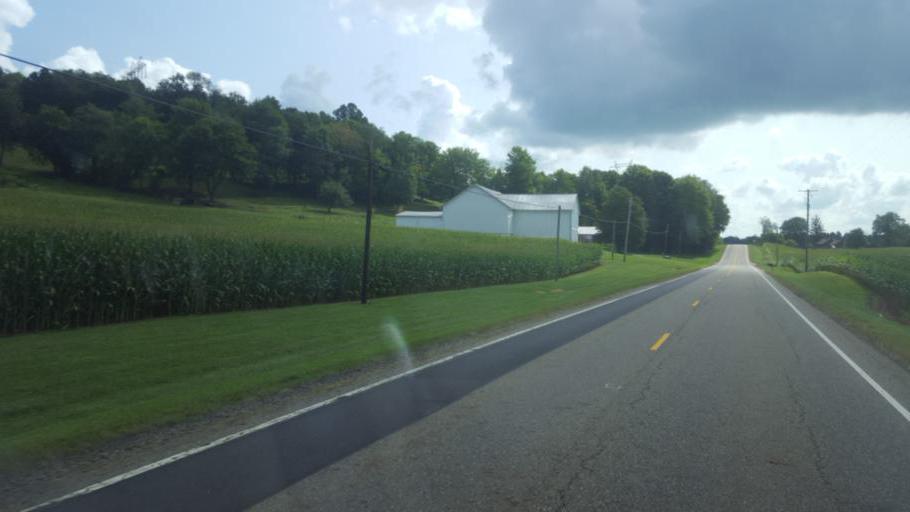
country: US
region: Ohio
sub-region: Stark County
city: Minerva
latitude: 40.7952
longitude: -81.1343
